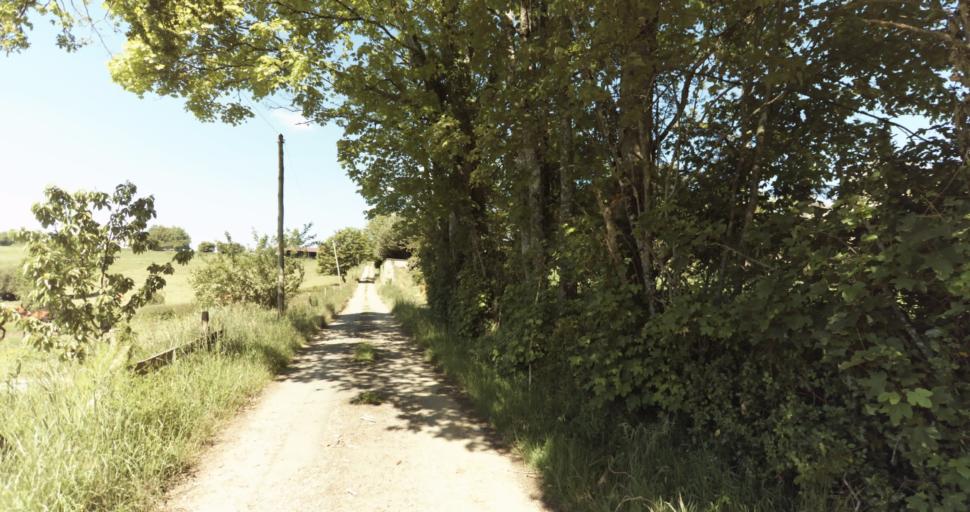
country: FR
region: Limousin
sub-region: Departement de la Haute-Vienne
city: Le Vigen
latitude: 45.7224
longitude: 1.3023
